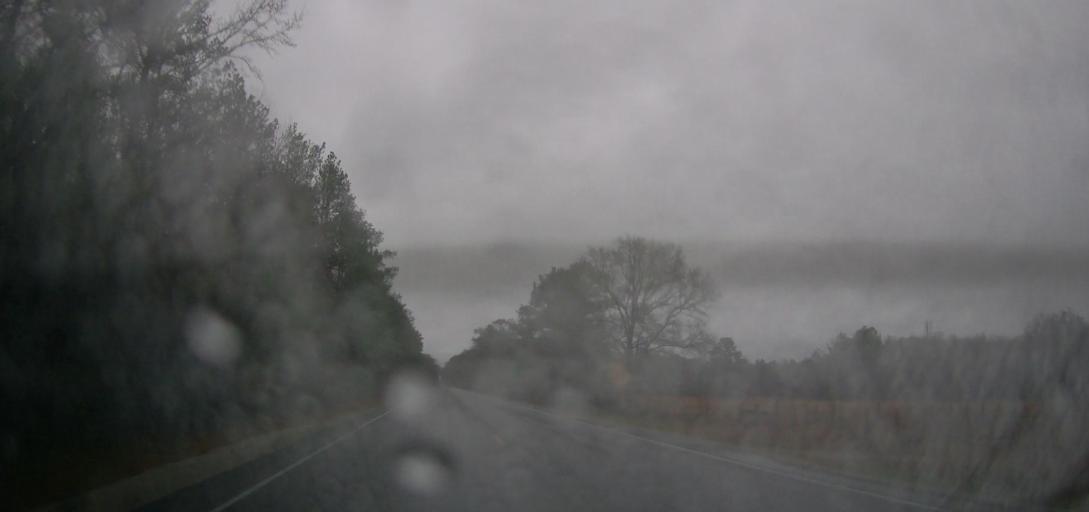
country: US
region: Alabama
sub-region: Autauga County
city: Pine Level
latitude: 32.5711
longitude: -86.6792
